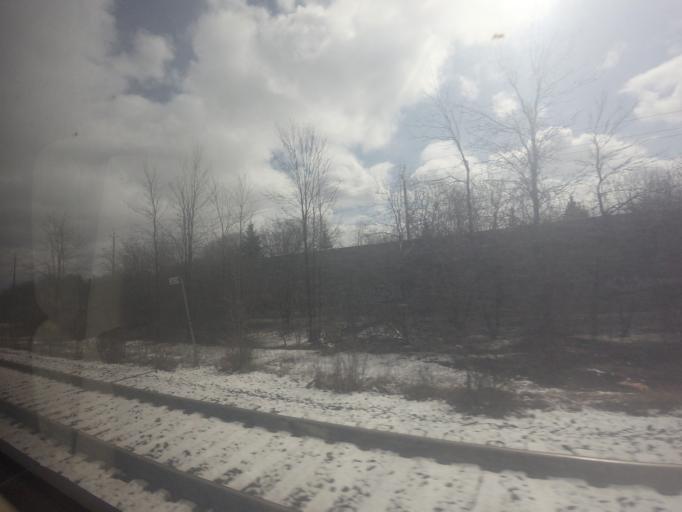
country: CA
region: Ontario
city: Ajax
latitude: 43.8538
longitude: -79.0155
